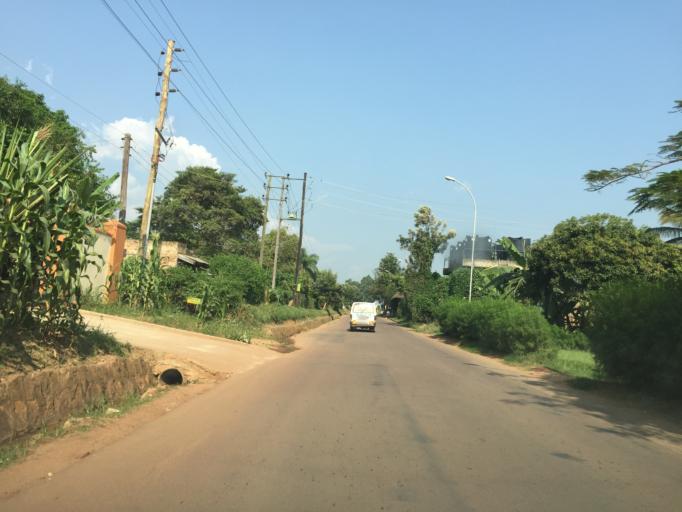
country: UG
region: Central Region
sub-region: Kampala District
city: Kampala
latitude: 0.2399
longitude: 32.6230
